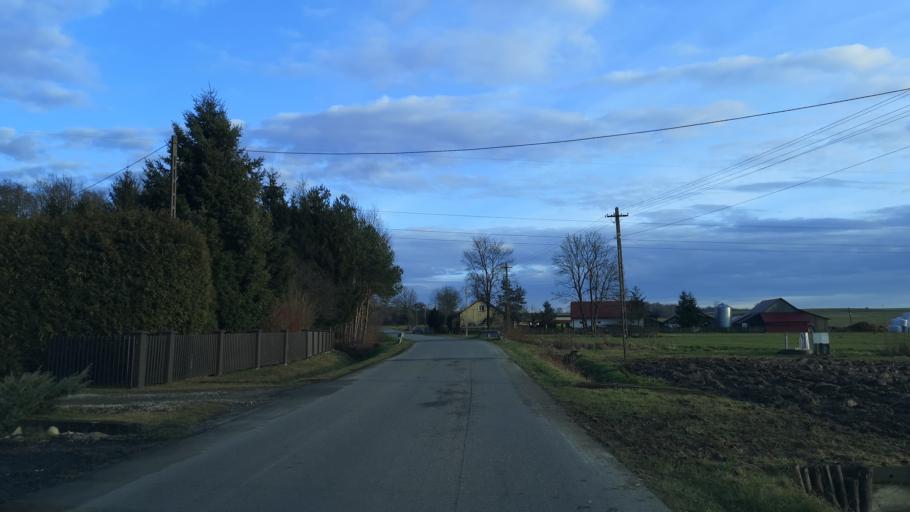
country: PL
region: Subcarpathian Voivodeship
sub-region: Powiat przeworski
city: Sieniawa
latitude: 50.2544
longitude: 22.6090
